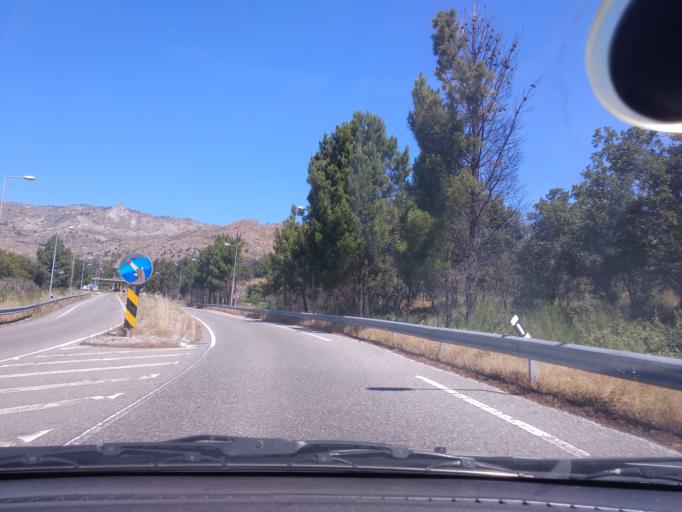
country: PT
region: Castelo Branco
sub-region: Concelho do Fundao
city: Fundao
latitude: 40.0752
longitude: -7.4742
